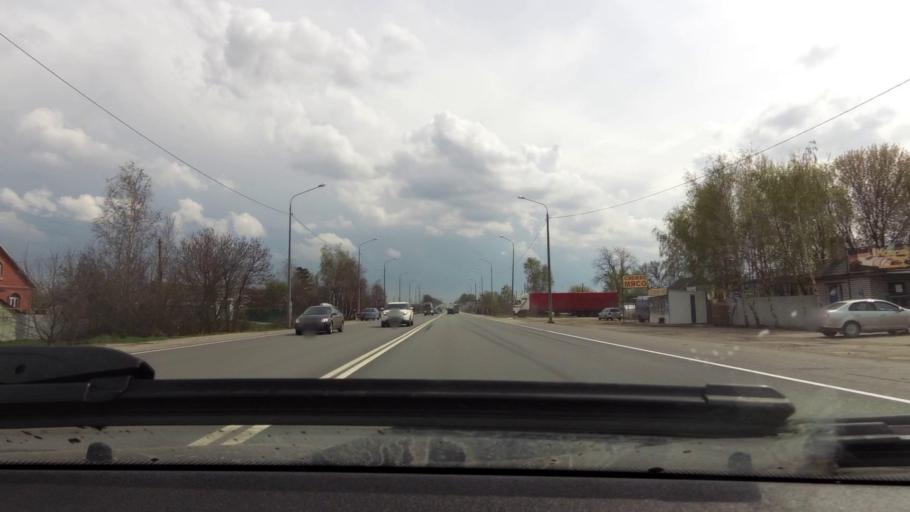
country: RU
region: Rjazan
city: Bagramovo
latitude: 54.7322
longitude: 39.4602
